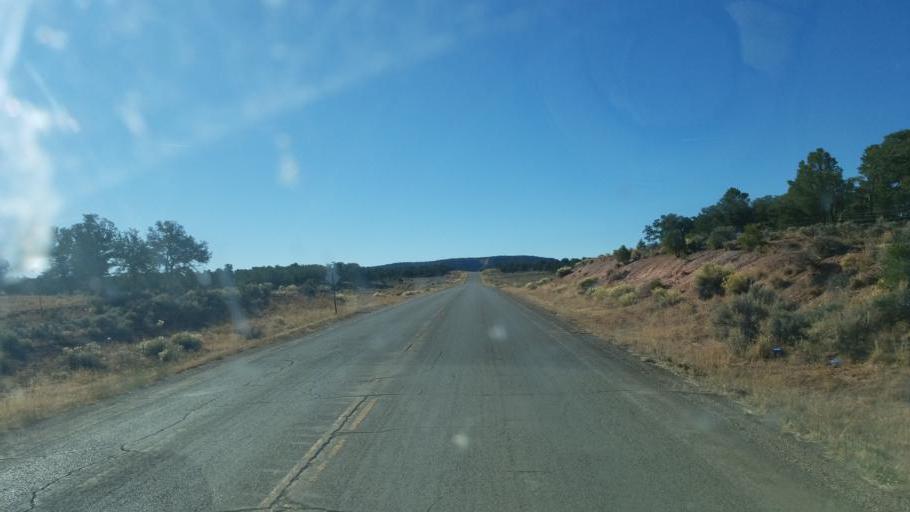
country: US
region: New Mexico
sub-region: McKinley County
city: Navajo
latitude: 35.9957
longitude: -109.0171
